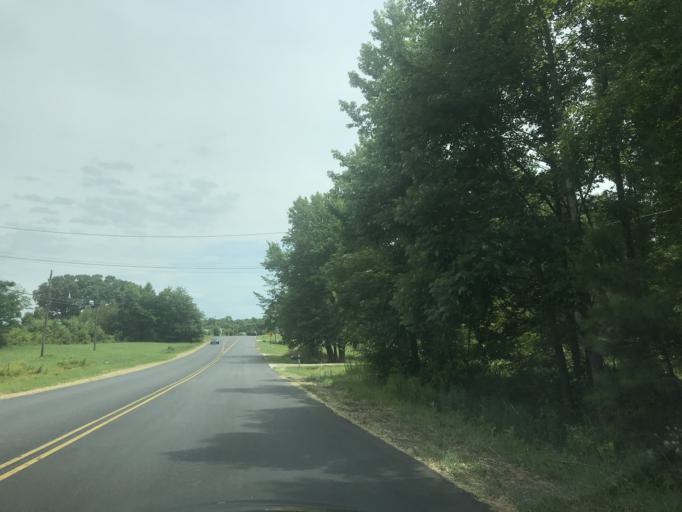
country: US
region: North Carolina
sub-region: Vance County
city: South Henderson
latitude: 36.2982
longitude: -78.4063
